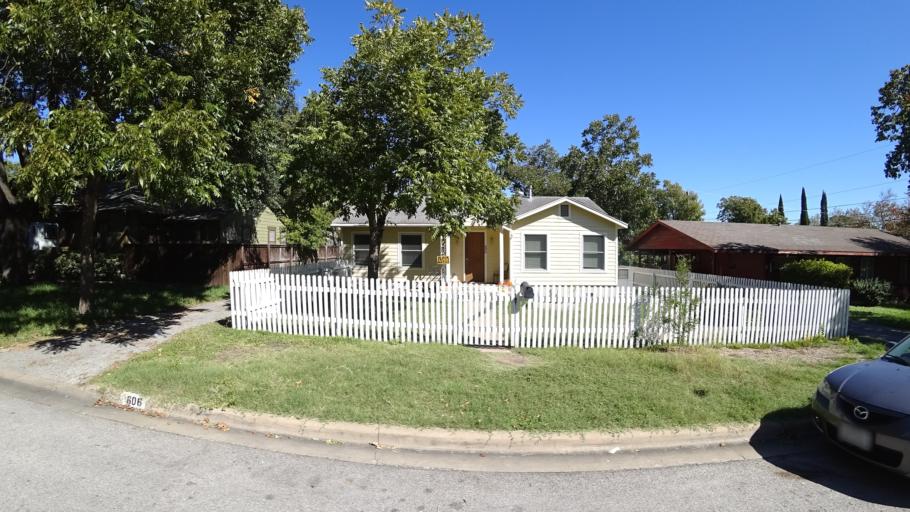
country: US
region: Texas
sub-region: Travis County
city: Austin
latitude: 30.3188
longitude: -97.7286
